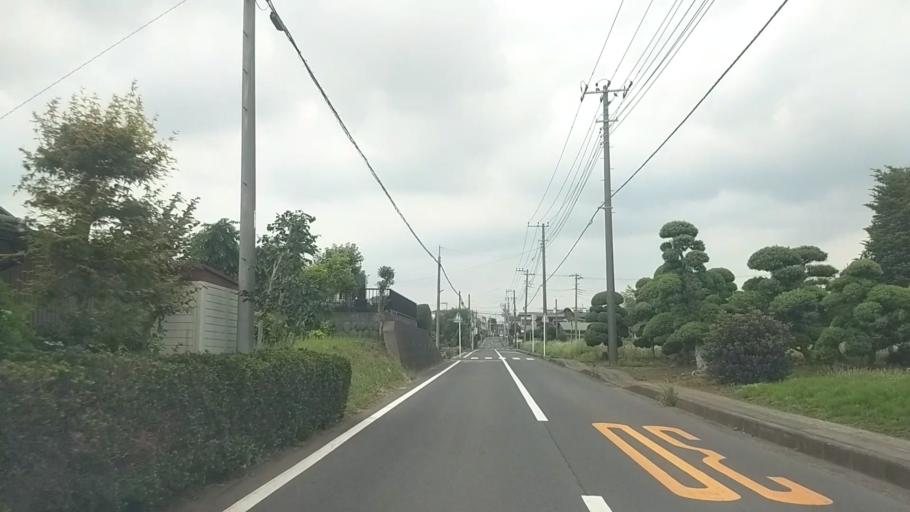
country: JP
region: Kanagawa
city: Atsugi
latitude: 35.3974
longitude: 139.4164
